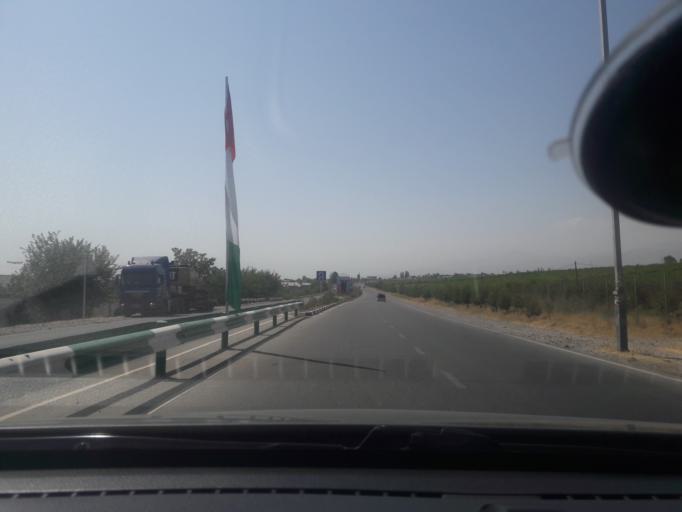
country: TJ
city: Shahrinav
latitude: 38.5613
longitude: 68.4363
